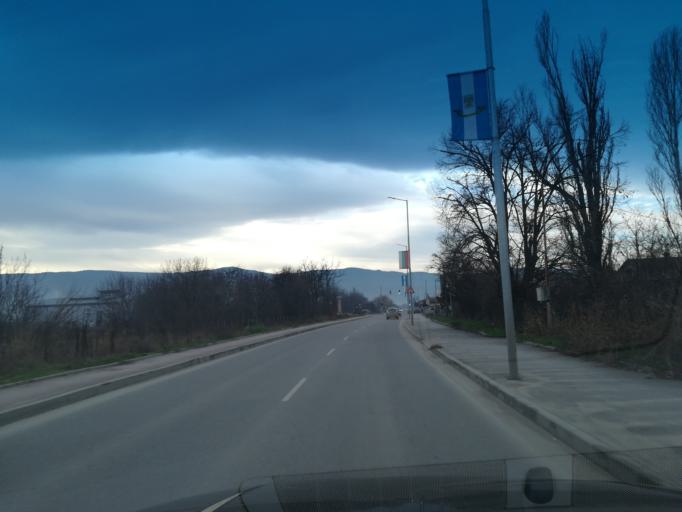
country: BG
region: Plovdiv
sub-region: Obshtina Plovdiv
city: Plovdiv
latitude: 42.1172
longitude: 24.7135
